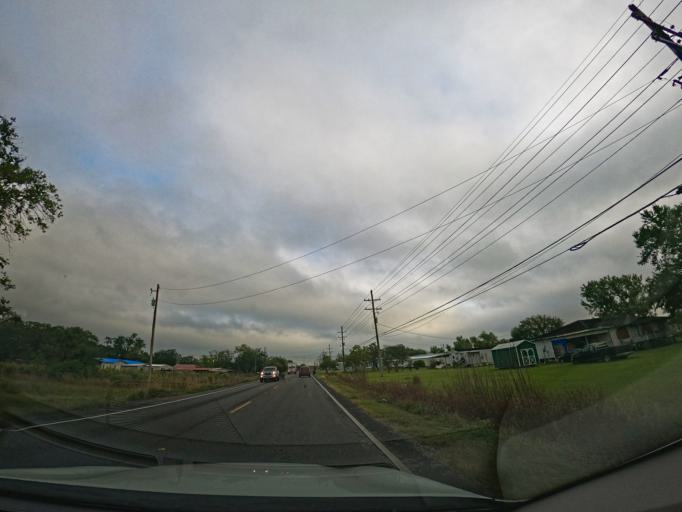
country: US
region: Louisiana
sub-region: Terrebonne Parish
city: Presquille
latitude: 29.5135
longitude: -90.6756
